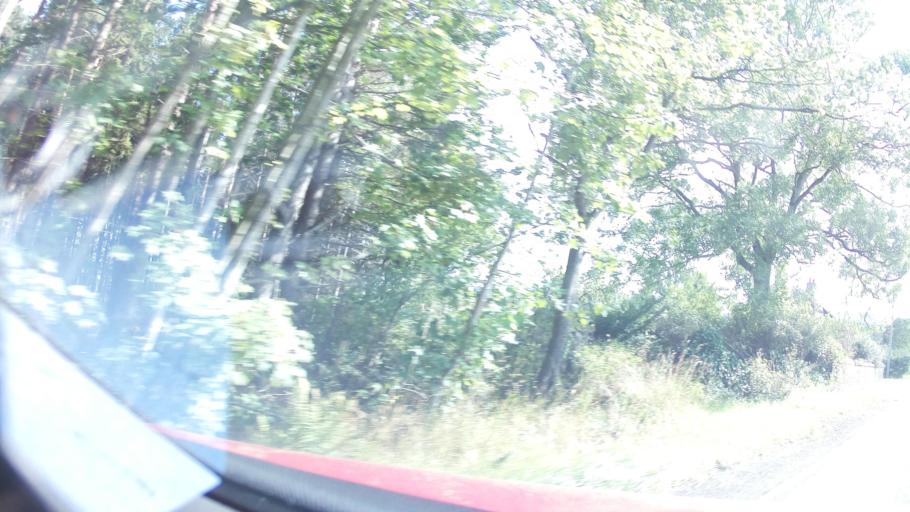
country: GB
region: England
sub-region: Northumberland
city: Healey
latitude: 54.9037
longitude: -1.9493
